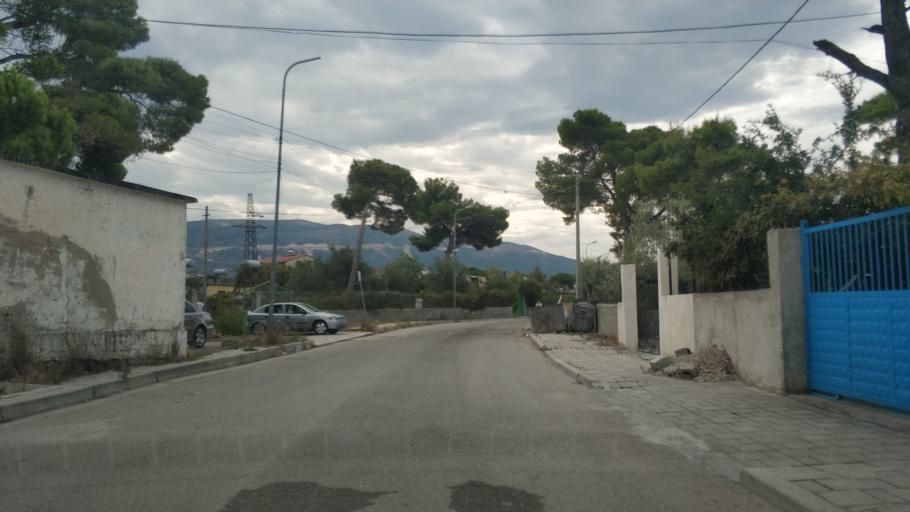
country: AL
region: Vlore
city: Vlore
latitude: 40.4606
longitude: 19.4688
